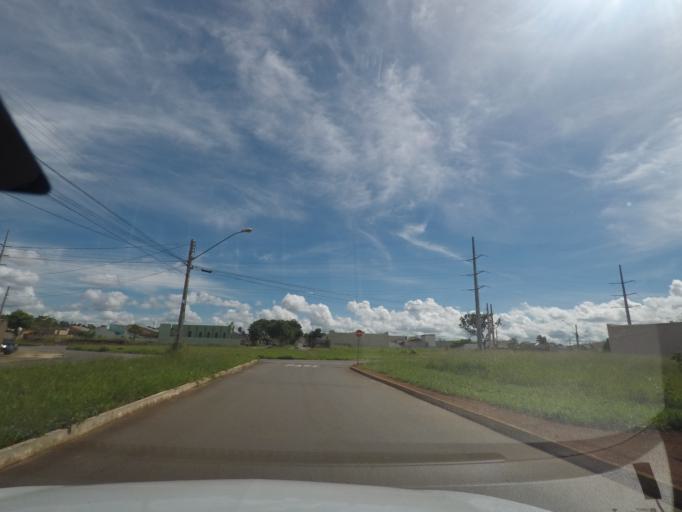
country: BR
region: Goias
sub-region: Goiania
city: Goiania
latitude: -16.7211
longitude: -49.3461
